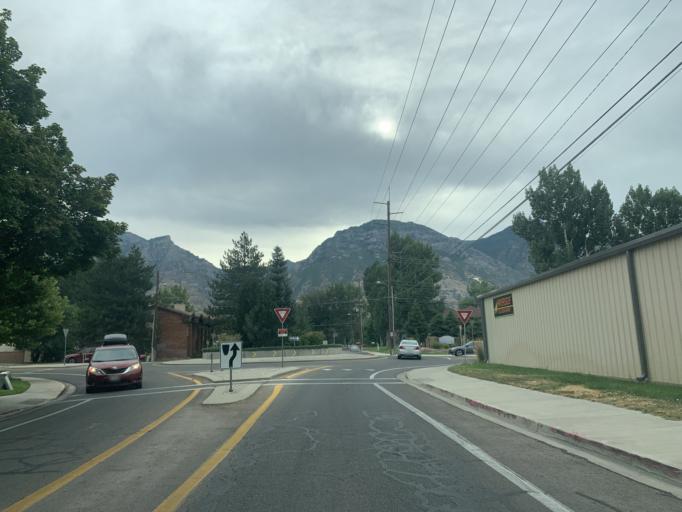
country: US
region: Utah
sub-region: Utah County
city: Provo
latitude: 40.2570
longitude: -111.6686
